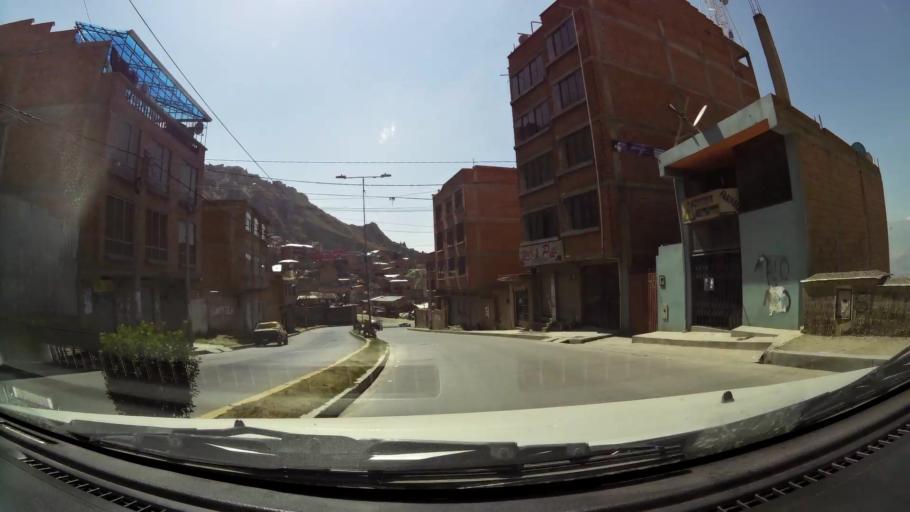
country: BO
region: La Paz
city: La Paz
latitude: -16.5329
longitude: -68.1394
